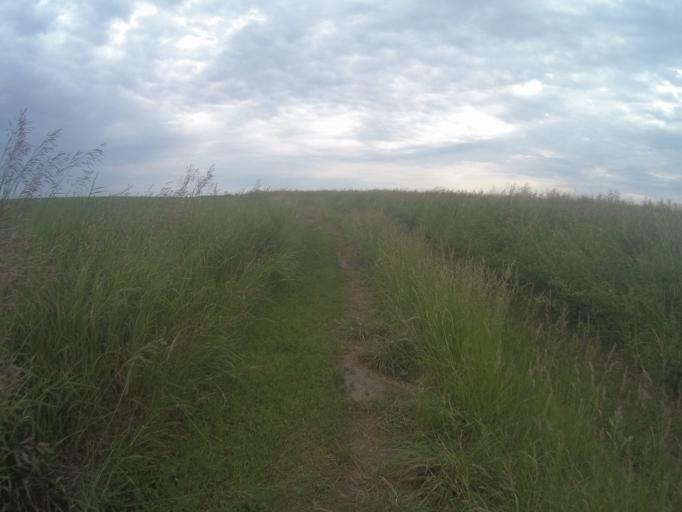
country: RU
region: Vladimir
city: Bogolyubovo
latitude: 56.2288
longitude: 40.4719
